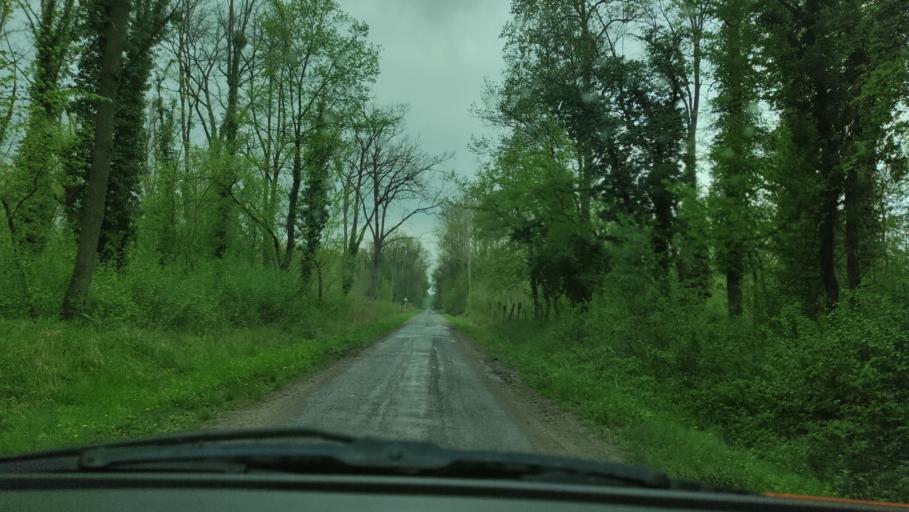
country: HU
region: Baranya
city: Mohacs
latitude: 45.9103
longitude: 18.7309
